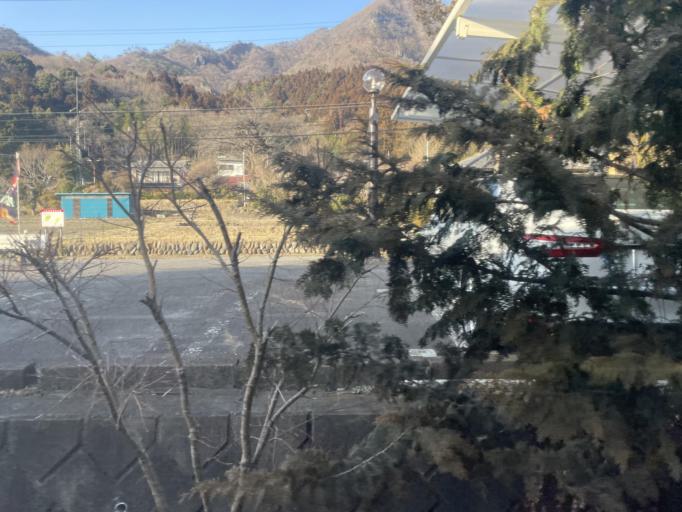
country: JP
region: Gunma
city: Nakanojomachi
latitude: 36.5660
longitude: 138.8913
